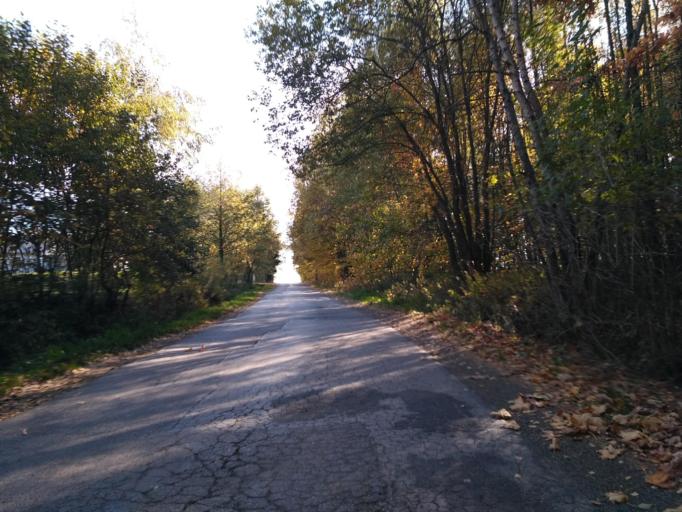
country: PL
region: Subcarpathian Voivodeship
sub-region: Powiat ropczycko-sedziszowski
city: Iwierzyce
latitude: 50.0427
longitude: 21.7746
